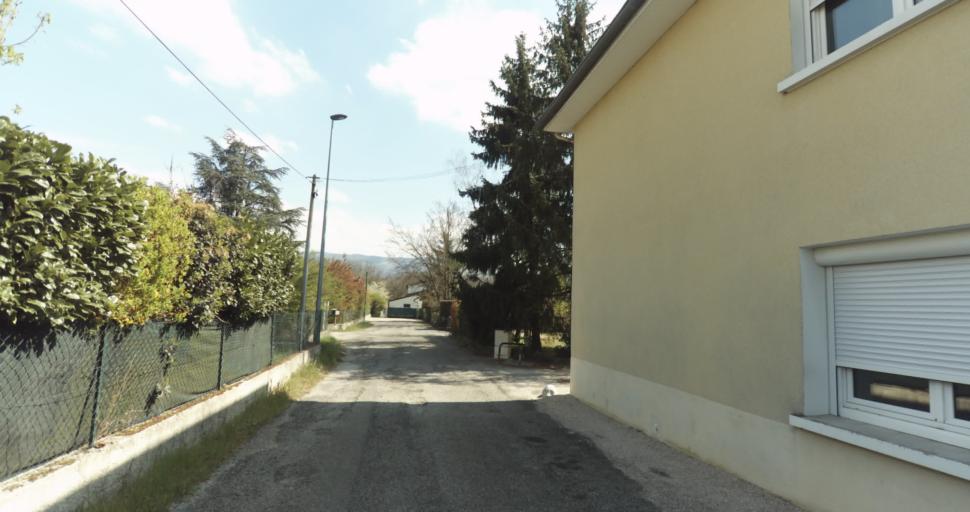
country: FR
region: Rhone-Alpes
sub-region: Departement de l'Isere
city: Saint-Marcellin
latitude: 45.1471
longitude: 5.3158
